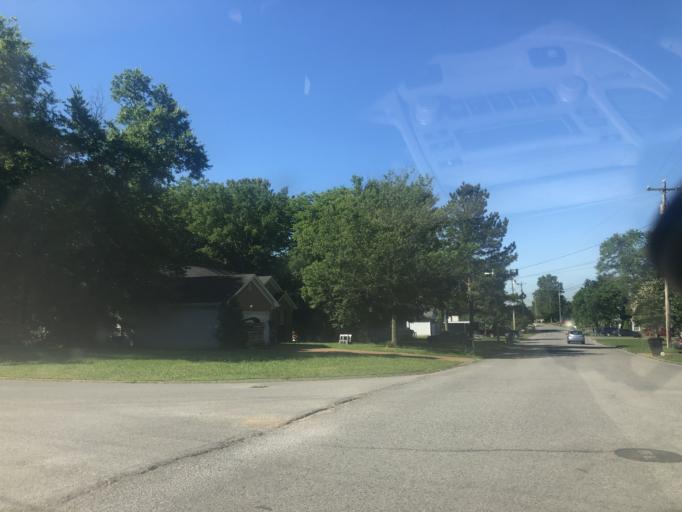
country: US
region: Tennessee
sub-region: Davidson County
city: Lakewood
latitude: 36.2422
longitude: -86.6674
